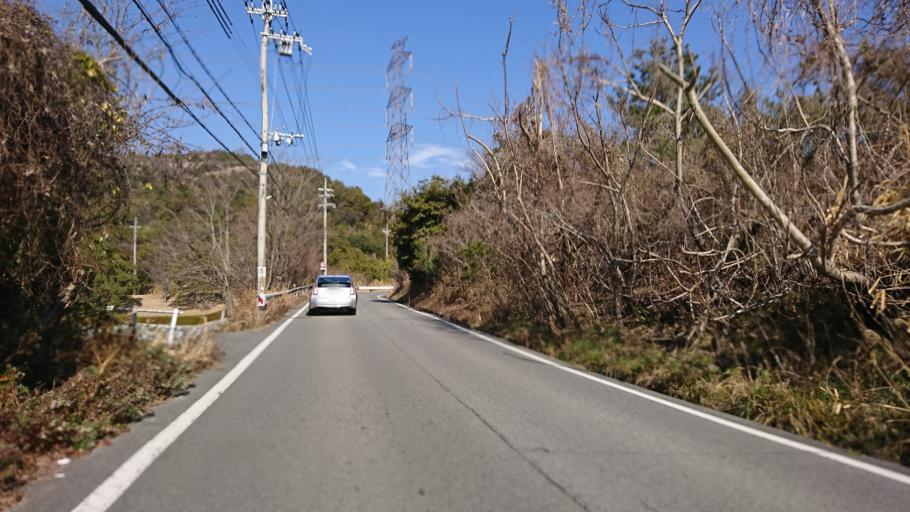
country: JP
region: Hyogo
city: Kakogawacho-honmachi
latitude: 34.7968
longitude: 134.8396
